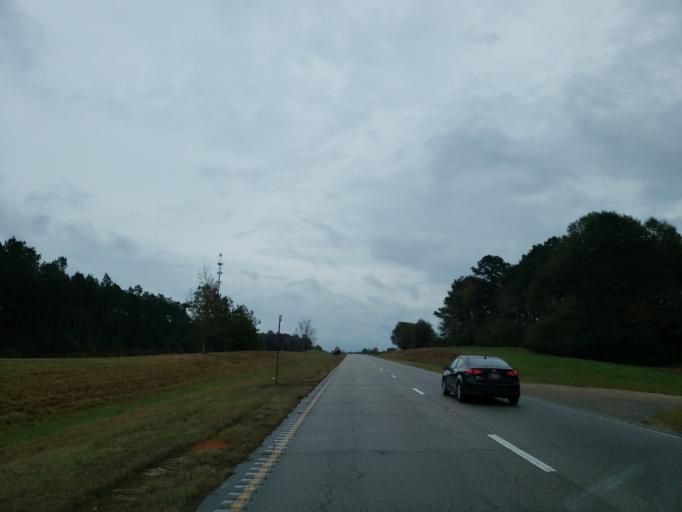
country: US
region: Mississippi
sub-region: Jones County
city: Sharon
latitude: 31.7047
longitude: -88.9255
